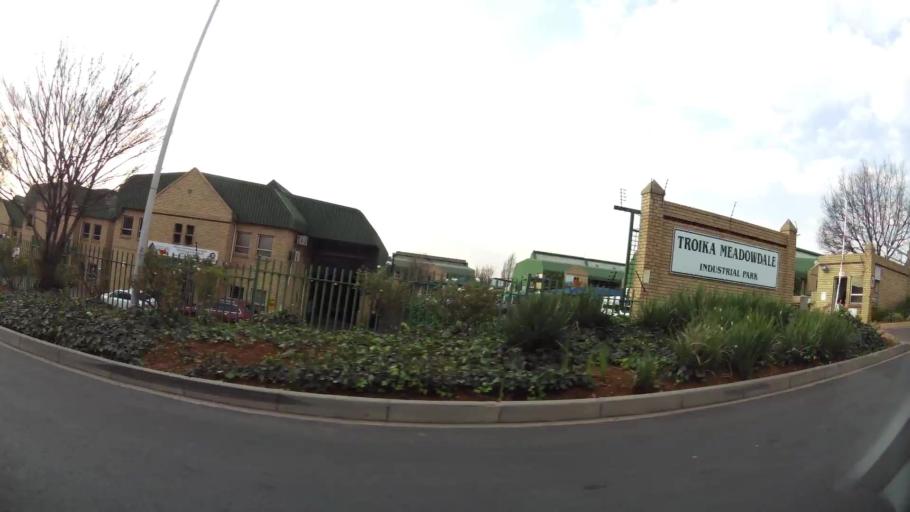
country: ZA
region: Gauteng
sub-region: City of Johannesburg Metropolitan Municipality
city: Modderfontein
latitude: -26.1525
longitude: 28.1826
